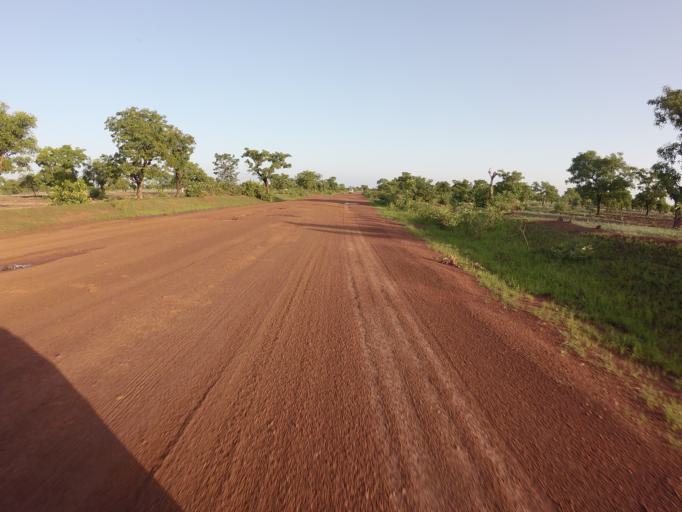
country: TG
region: Savanes
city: Sansanne-Mango
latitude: 10.2734
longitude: -0.0824
